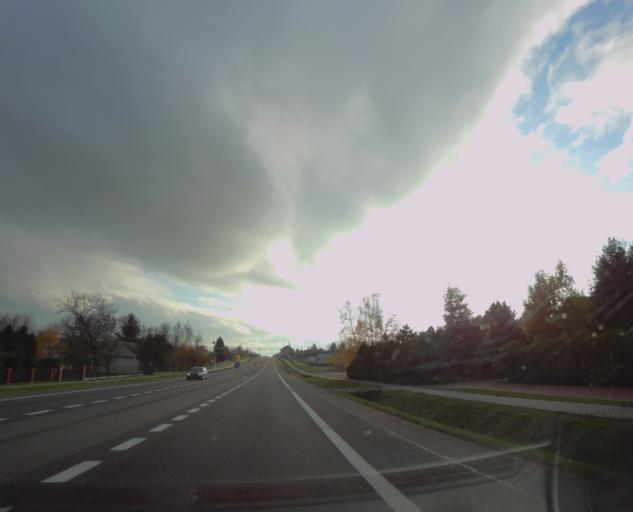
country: PL
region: Subcarpathian Voivodeship
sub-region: Powiat przemyski
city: Orly
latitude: 49.8788
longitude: 22.8134
